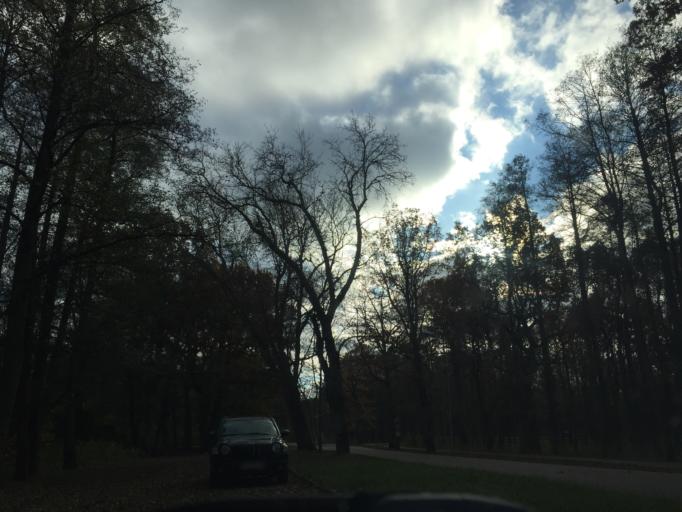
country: LV
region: Liepaja
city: Vec-Liepaja
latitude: 56.5461
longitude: 21.0793
